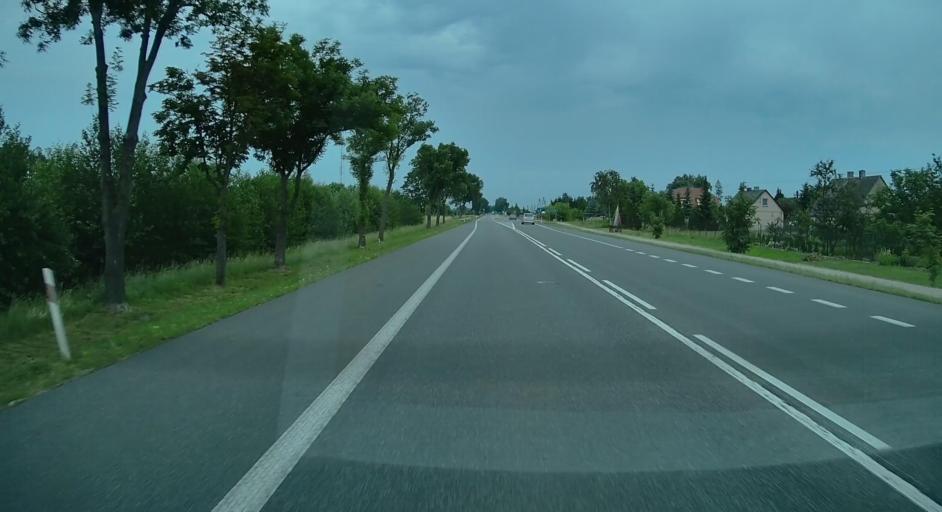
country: PL
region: Lublin Voivodeship
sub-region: Powiat lukowski
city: Trzebieszow
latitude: 52.0631
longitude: 22.5494
